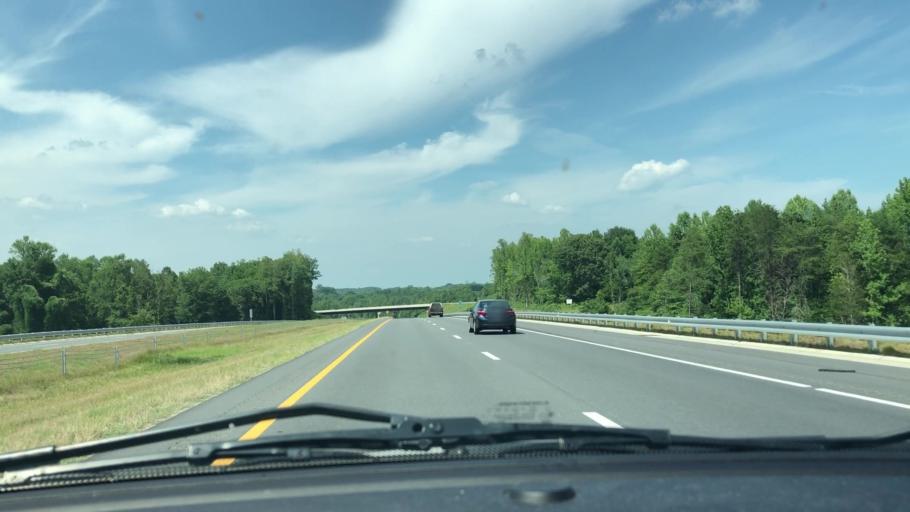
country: US
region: North Carolina
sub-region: Guilford County
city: Summerfield
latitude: 36.2205
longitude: -79.9148
